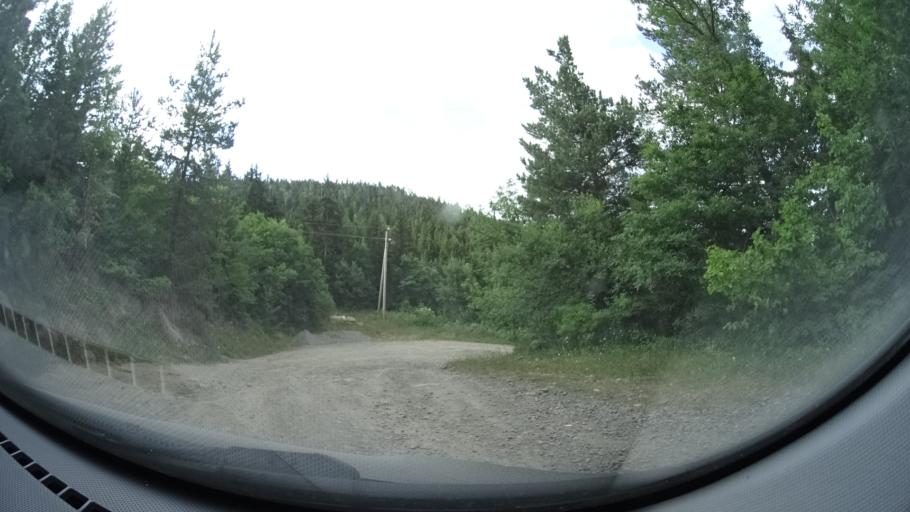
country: GE
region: Samtskhe-Javakheti
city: Adigeni
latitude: 41.6647
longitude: 42.6124
